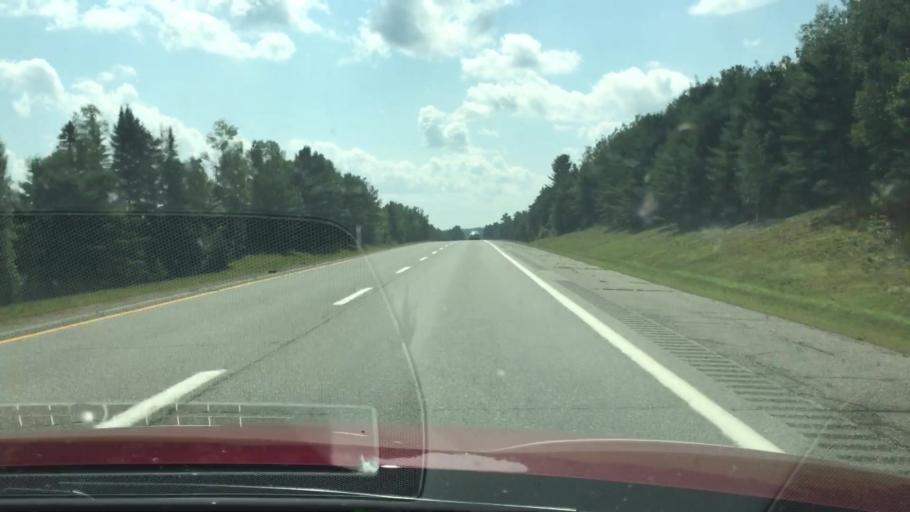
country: US
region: Maine
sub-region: Penobscot County
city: Medway
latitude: 45.4967
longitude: -68.5619
